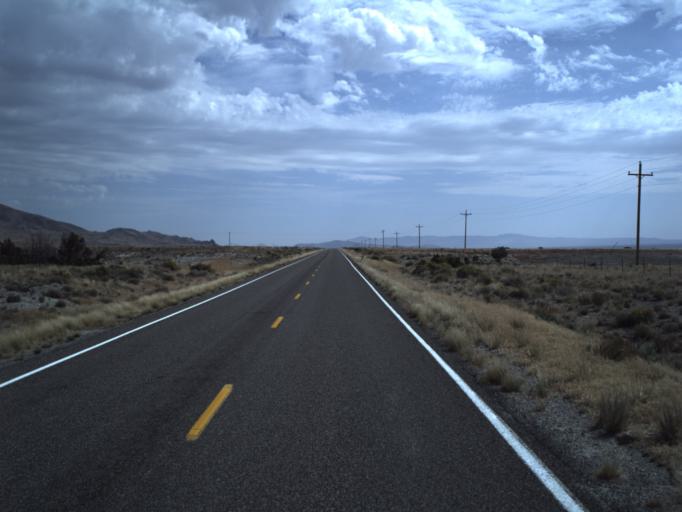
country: US
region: Utah
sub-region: Tooele County
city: Wendover
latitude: 41.4342
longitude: -113.7683
